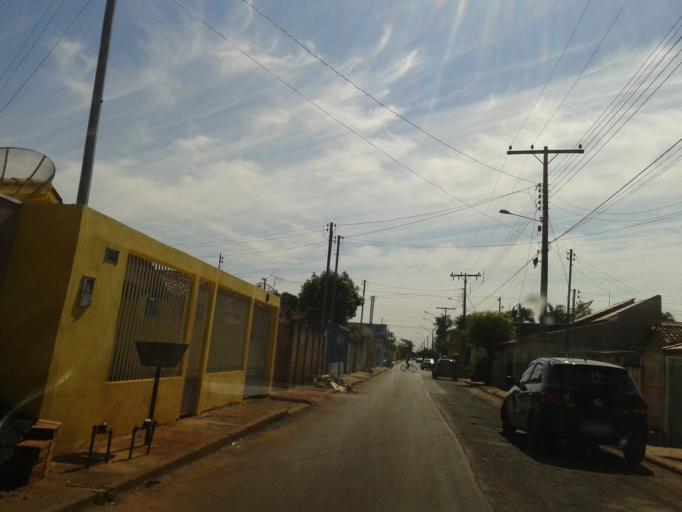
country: BR
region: Minas Gerais
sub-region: Santa Vitoria
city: Santa Vitoria
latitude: -19.0009
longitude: -50.5496
